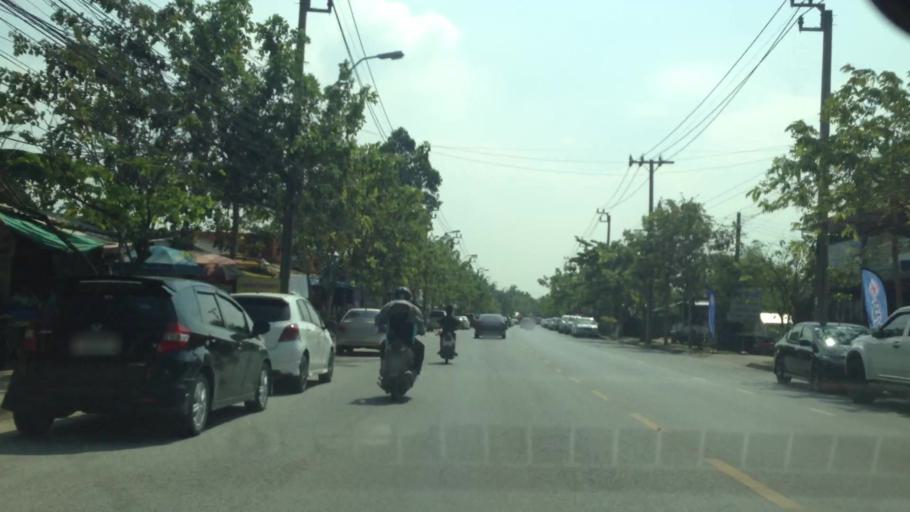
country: TH
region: Bangkok
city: Bang Khen
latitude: 13.8891
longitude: 100.6427
